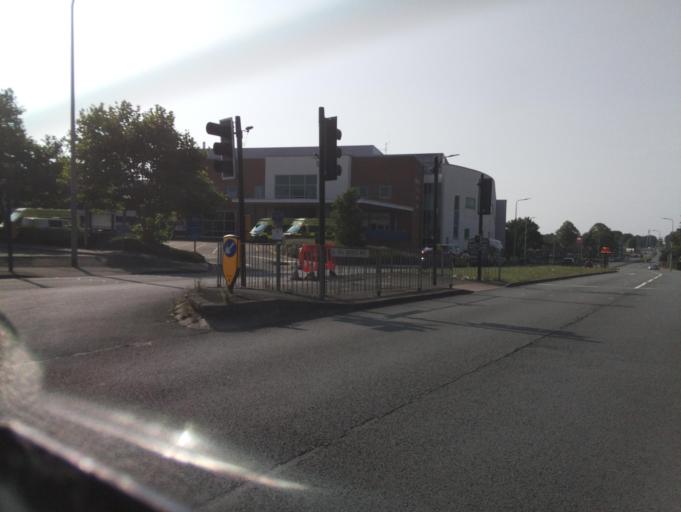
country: GB
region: England
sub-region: Sandwell
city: West Bromwich
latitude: 52.5294
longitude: -1.9898
